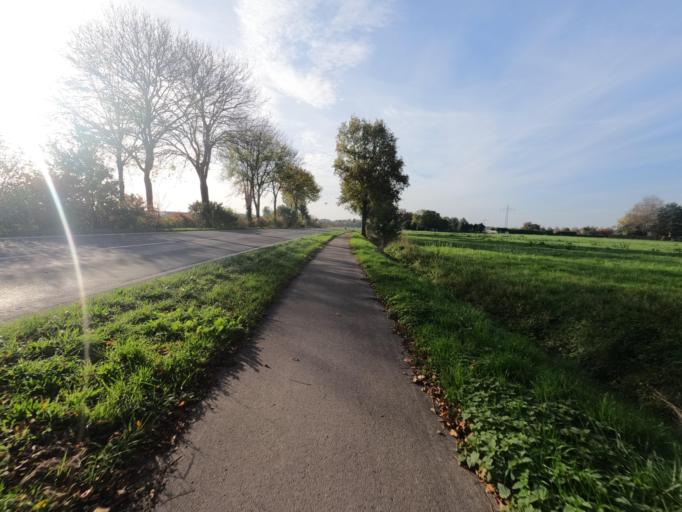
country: DE
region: North Rhine-Westphalia
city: Erkelenz
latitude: 51.0633
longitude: 6.3319
